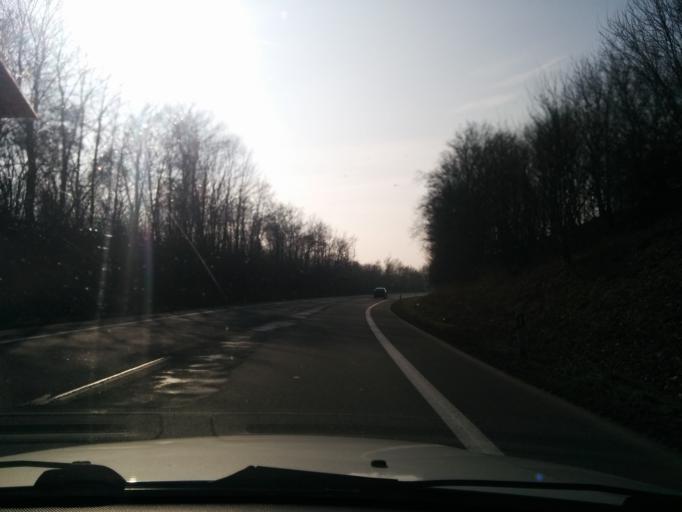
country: DE
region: North Rhine-Westphalia
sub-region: Regierungsbezirk Detmold
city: Steinheim
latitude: 51.8598
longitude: 9.1036
